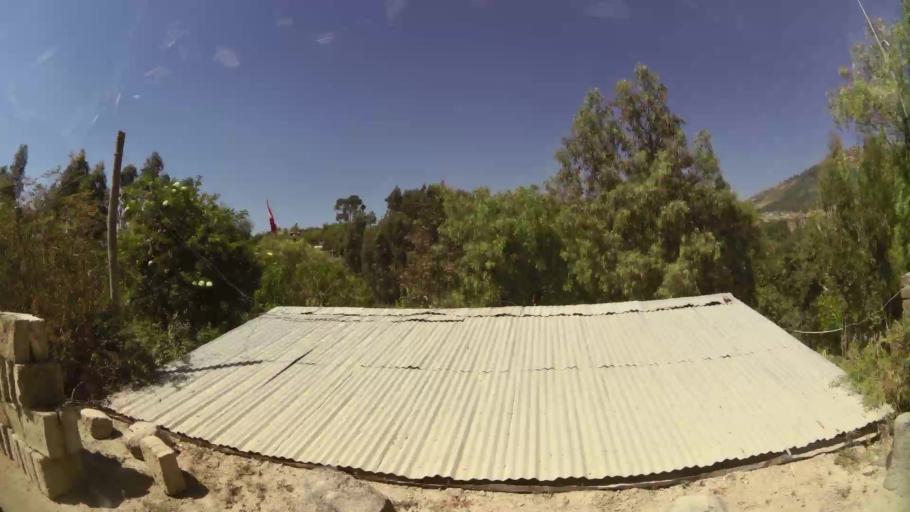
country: PE
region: Ayacucho
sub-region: Provincia de Huamanga
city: Carmen Alto
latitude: -13.1789
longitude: -74.2305
